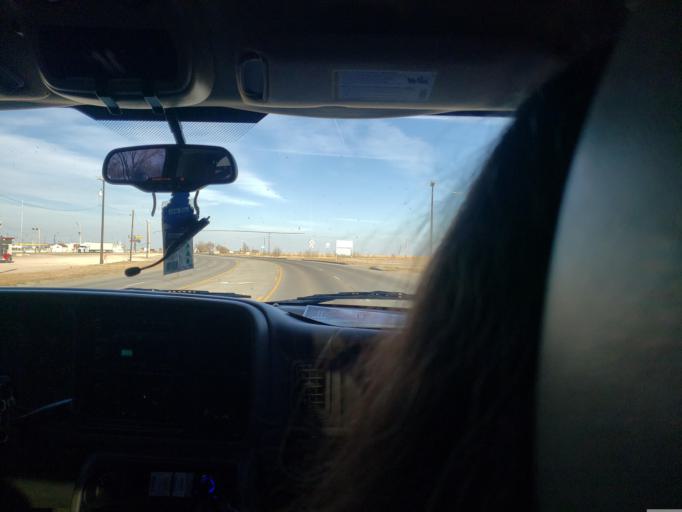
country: US
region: Oklahoma
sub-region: Texas County
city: Goodwell
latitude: 36.5019
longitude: -101.7784
